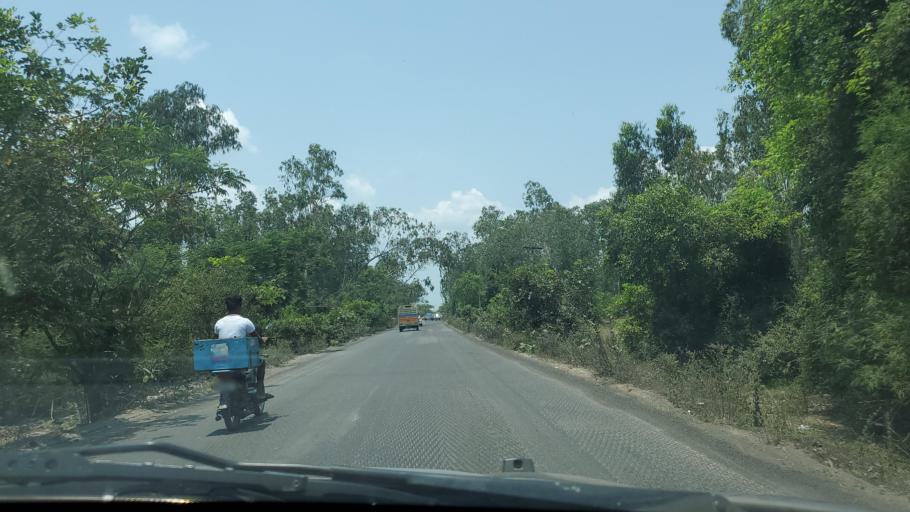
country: IN
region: Tamil Nadu
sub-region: Kancheepuram
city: Vengavasal
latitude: 12.8686
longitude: 80.1757
